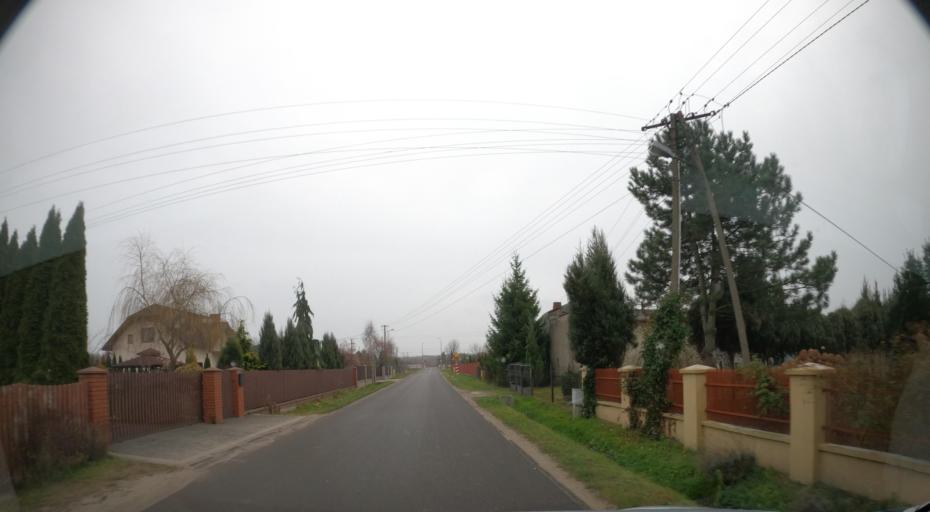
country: PL
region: Masovian Voivodeship
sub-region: Powiat radomski
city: Jastrzebia
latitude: 51.4154
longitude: 21.2506
